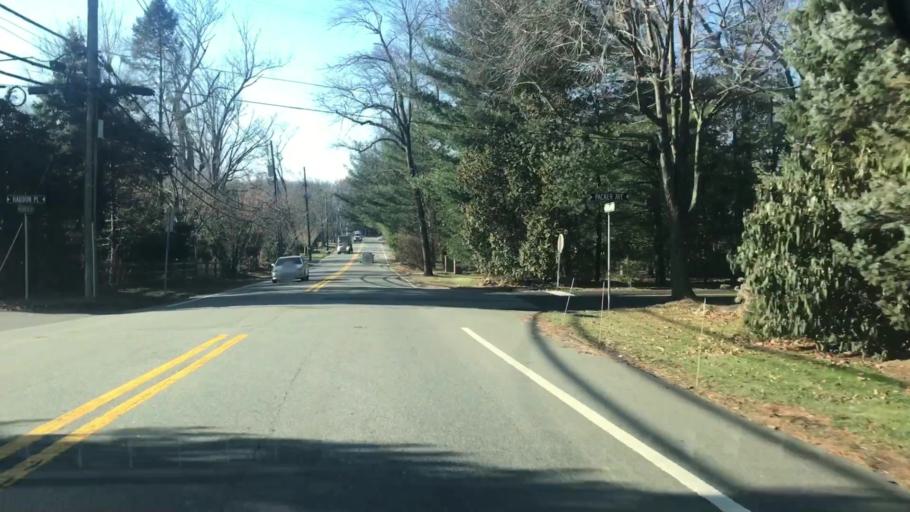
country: US
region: New Jersey
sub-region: Bergen County
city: Wyckoff
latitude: 41.0114
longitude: -74.1891
